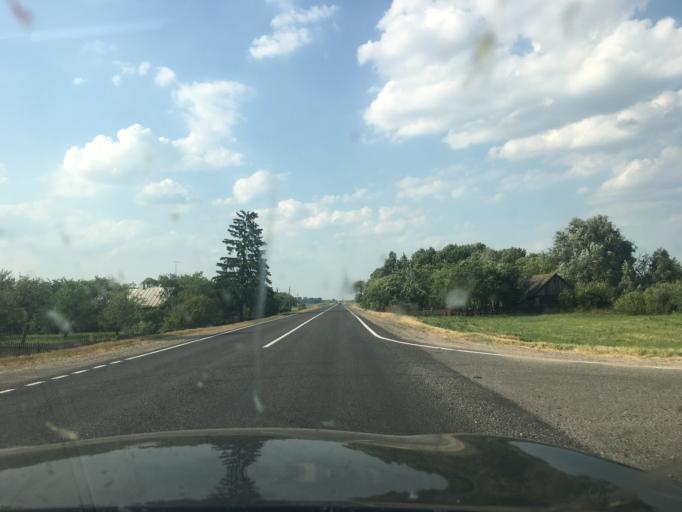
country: BY
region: Grodnenskaya
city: Indura
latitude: 53.3889
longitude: 23.9512
